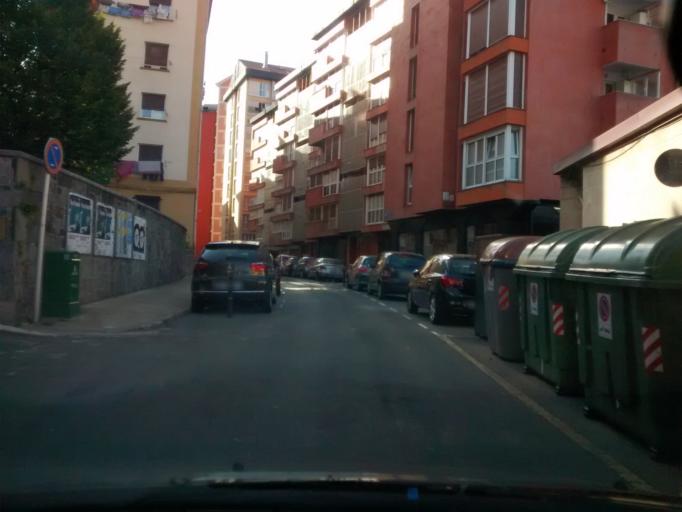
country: ES
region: Basque Country
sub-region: Provincia de Guipuzcoa
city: Eibar
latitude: 43.1825
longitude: -2.4755
